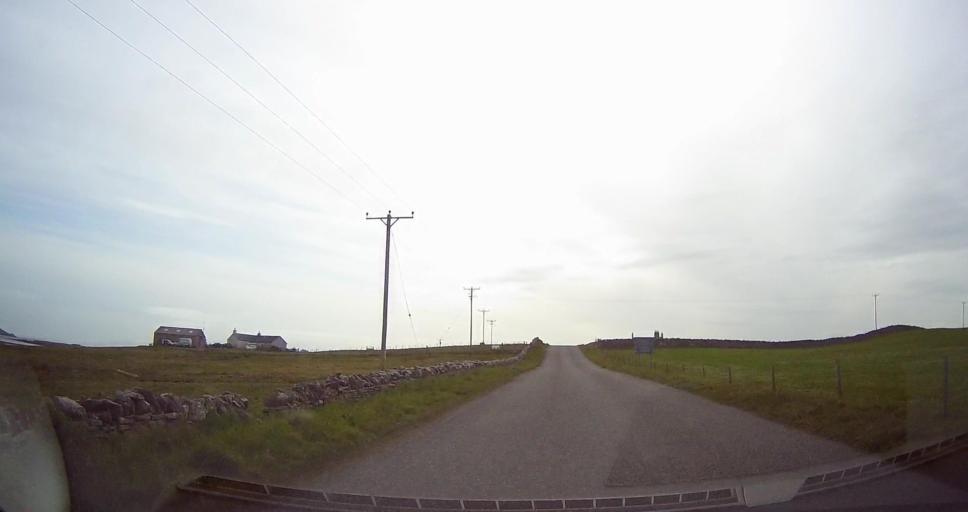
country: GB
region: Scotland
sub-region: Shetland Islands
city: Shetland
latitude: 60.1585
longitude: -1.1159
